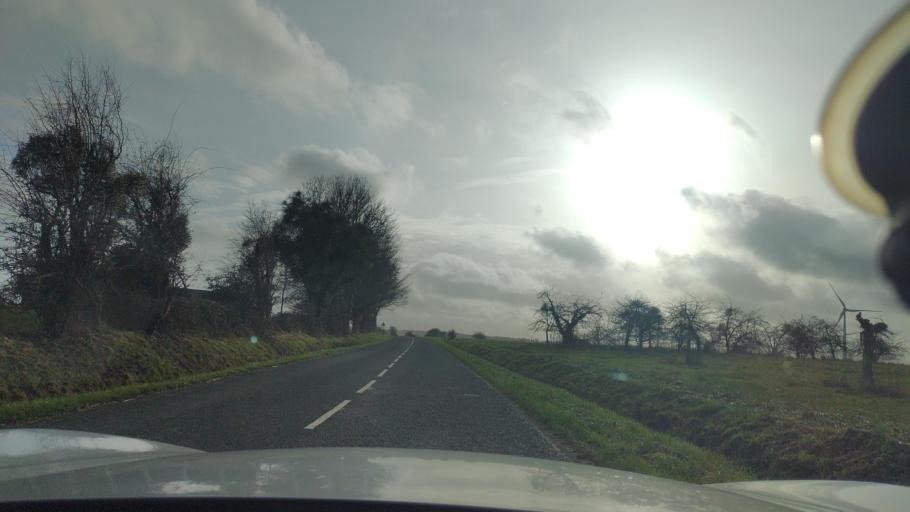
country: FR
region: Picardie
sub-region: Departement de la Somme
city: Beaucamps-le-Vieux
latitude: 49.8902
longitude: 1.8209
